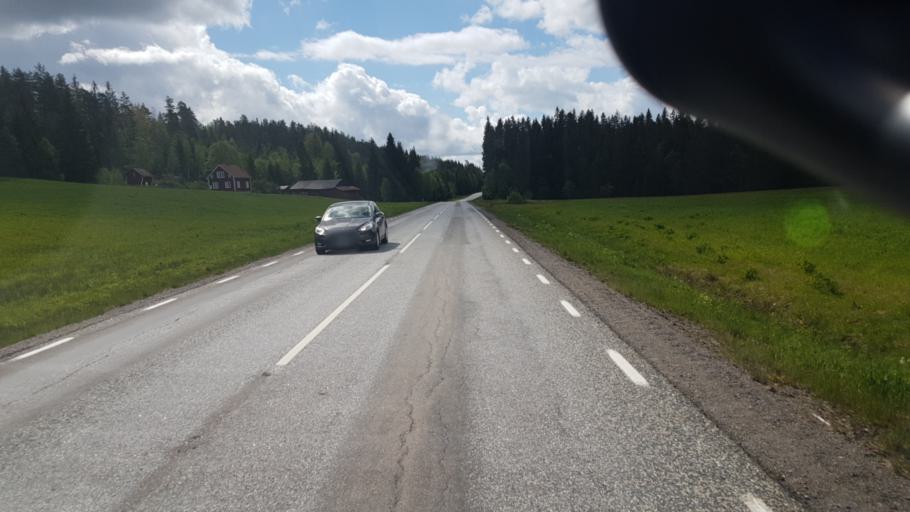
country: SE
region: Vaermland
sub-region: Arjangs Kommun
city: Arjaeng
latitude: 59.5715
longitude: 12.1235
